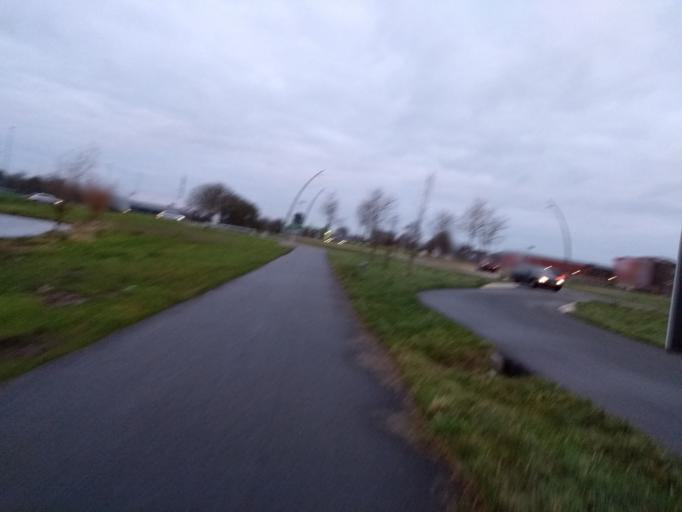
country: NL
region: Friesland
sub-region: Sudwest Fryslan
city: Sneek
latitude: 53.0168
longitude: 5.6541
